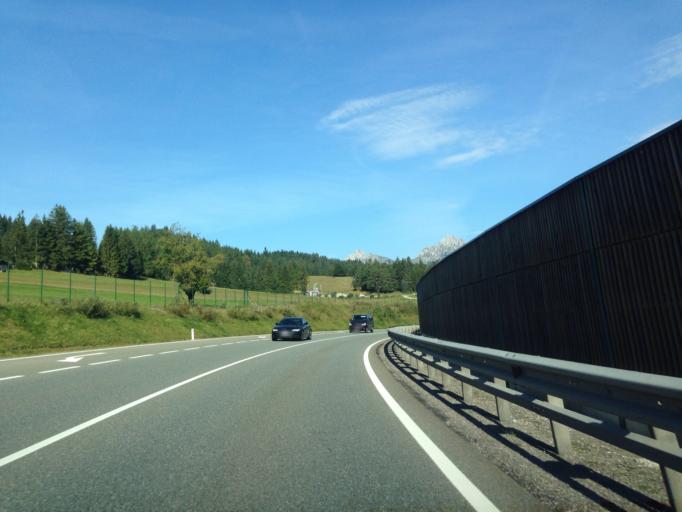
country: AT
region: Tyrol
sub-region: Politischer Bezirk Reutte
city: Heiterwang
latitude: 47.4477
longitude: 10.7355
